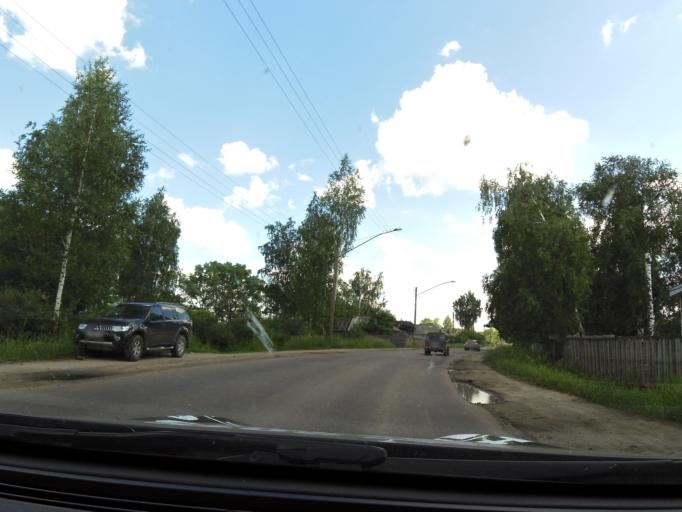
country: RU
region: Vologda
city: Vologda
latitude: 59.2391
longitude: 39.7954
